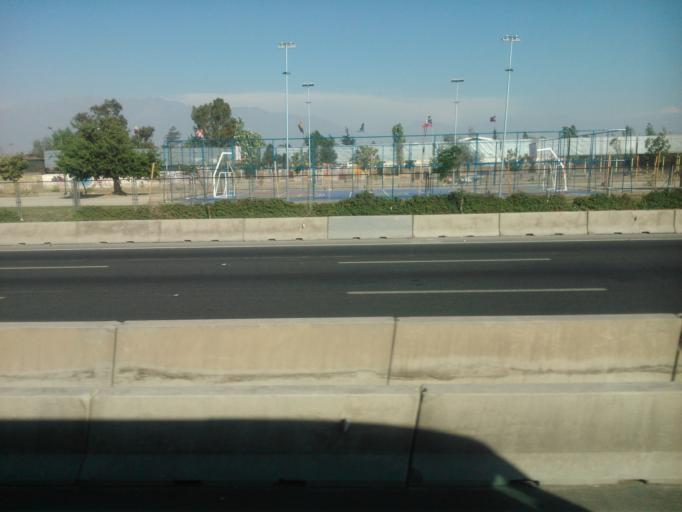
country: CL
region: Santiago Metropolitan
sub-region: Provincia de Santiago
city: Santiago
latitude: -33.4963
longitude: -70.6924
